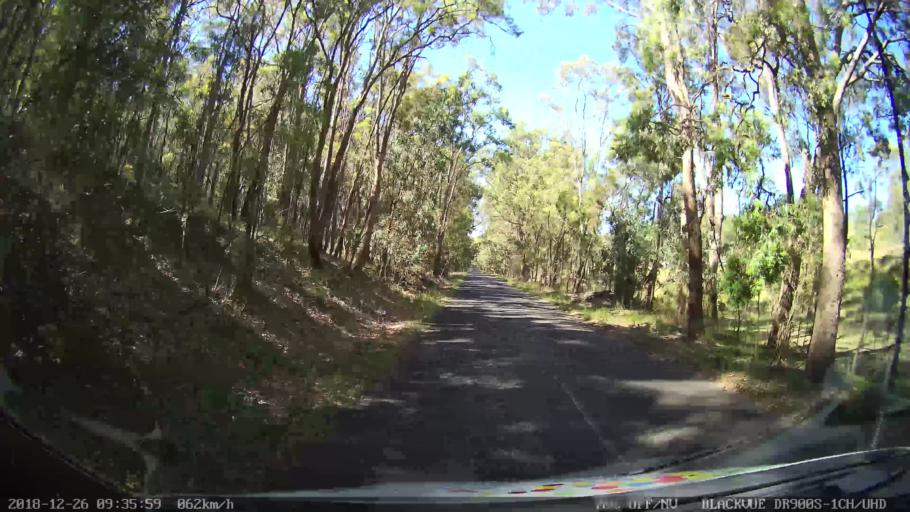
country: AU
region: New South Wales
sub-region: Mid-Western Regional
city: Kandos
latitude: -32.9199
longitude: 150.0411
